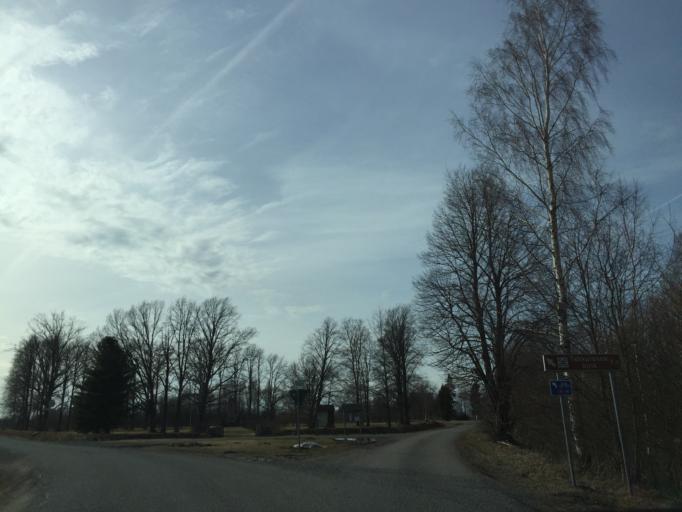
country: EE
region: Paernumaa
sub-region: Paernu linn
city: Parnu
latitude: 58.2467
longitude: 24.5043
